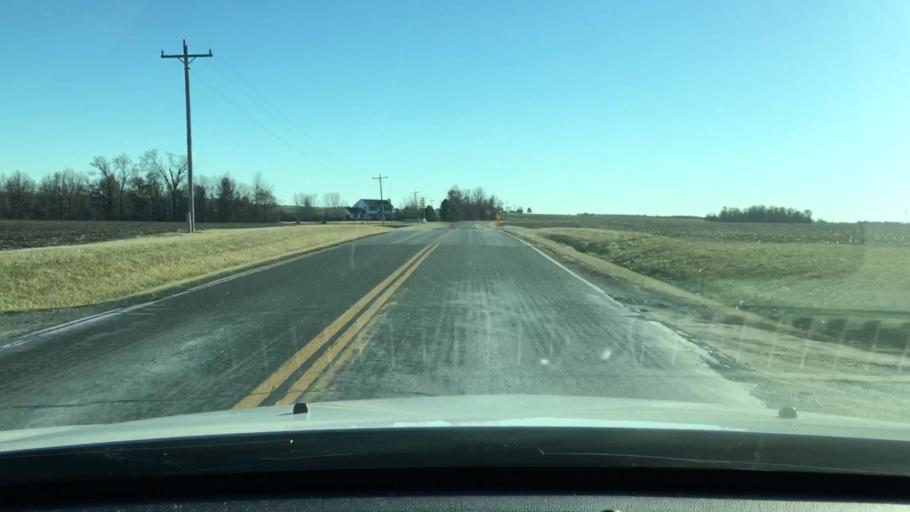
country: US
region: Missouri
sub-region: Audrain County
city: Mexico
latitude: 39.2398
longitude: -91.8387
